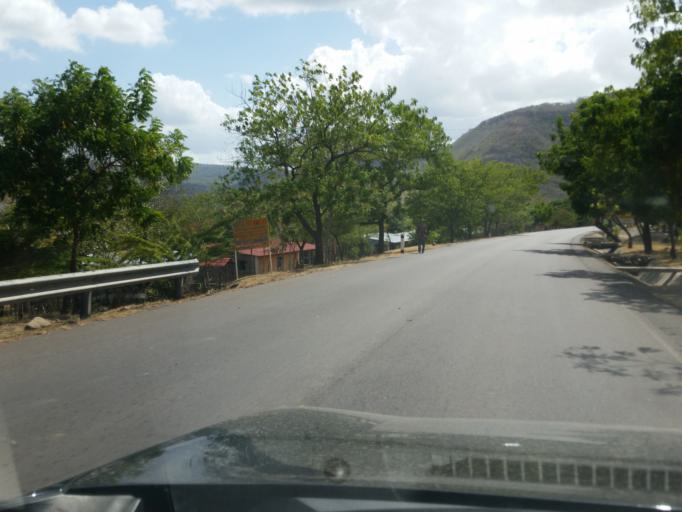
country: NI
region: Boaco
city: San Lorenzo
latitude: 12.2597
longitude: -85.6438
